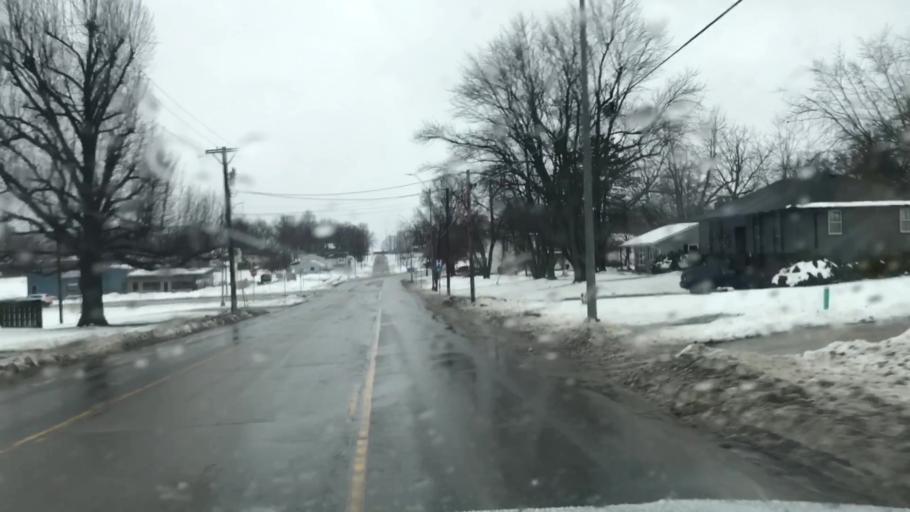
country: US
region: Missouri
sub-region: Clinton County
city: Cameron
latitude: 39.7328
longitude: -94.2360
